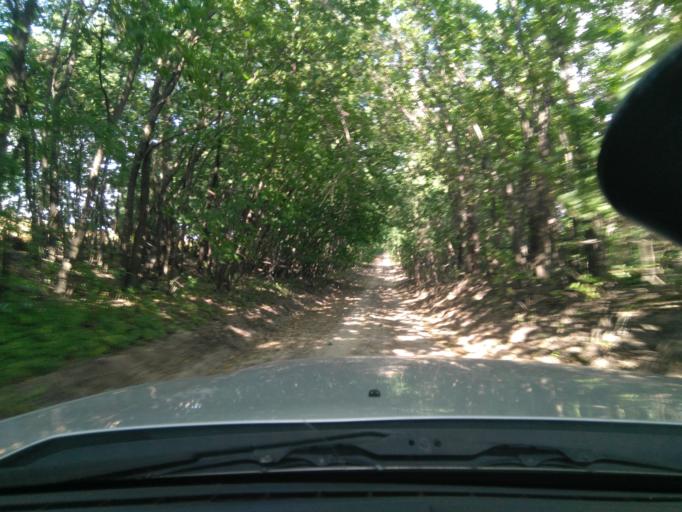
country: HU
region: Fejer
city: Bicske
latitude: 47.4433
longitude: 18.6502
